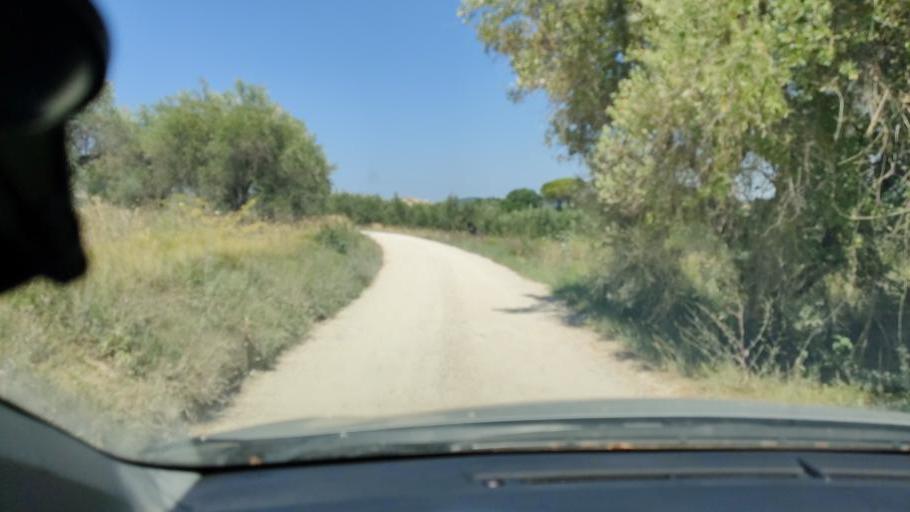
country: IT
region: Umbria
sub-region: Provincia di Terni
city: Fornole
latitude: 42.5456
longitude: 12.4399
